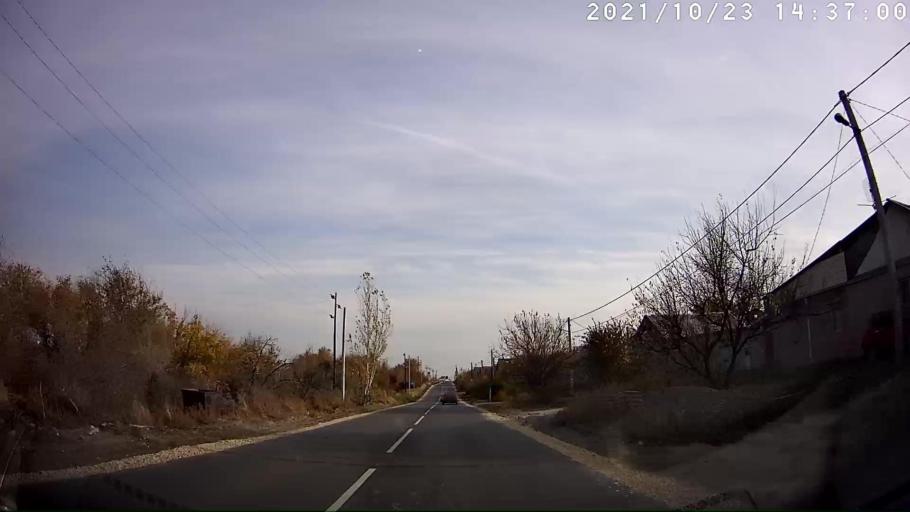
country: RU
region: Volgograd
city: Krasnoslobodsk
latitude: 48.4998
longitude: 44.5457
